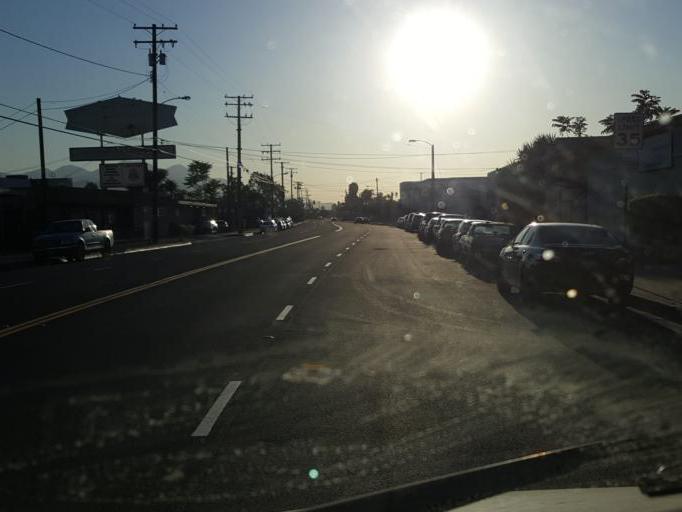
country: US
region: California
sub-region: Los Angeles County
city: Baldwin Park
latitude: 34.0884
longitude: -117.9531
